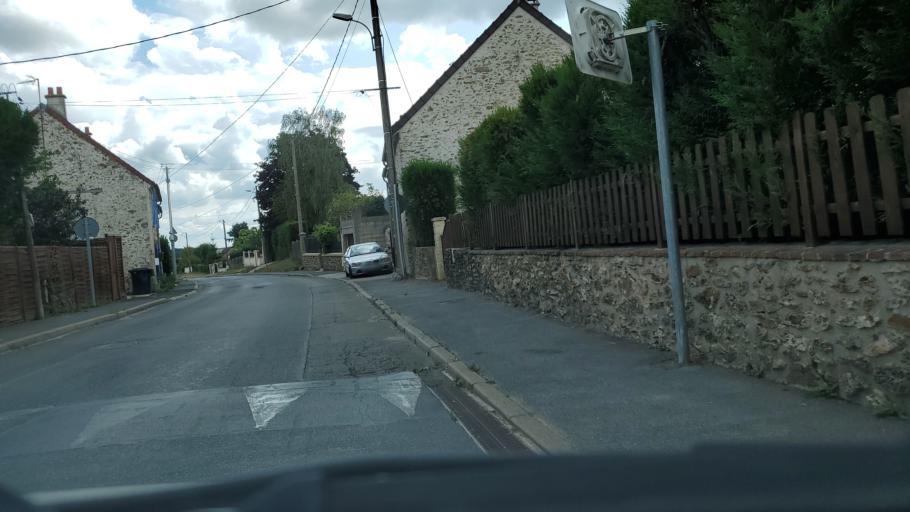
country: FR
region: Ile-de-France
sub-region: Departement de Seine-et-Marne
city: Mouroux
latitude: 48.8307
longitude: 3.0351
